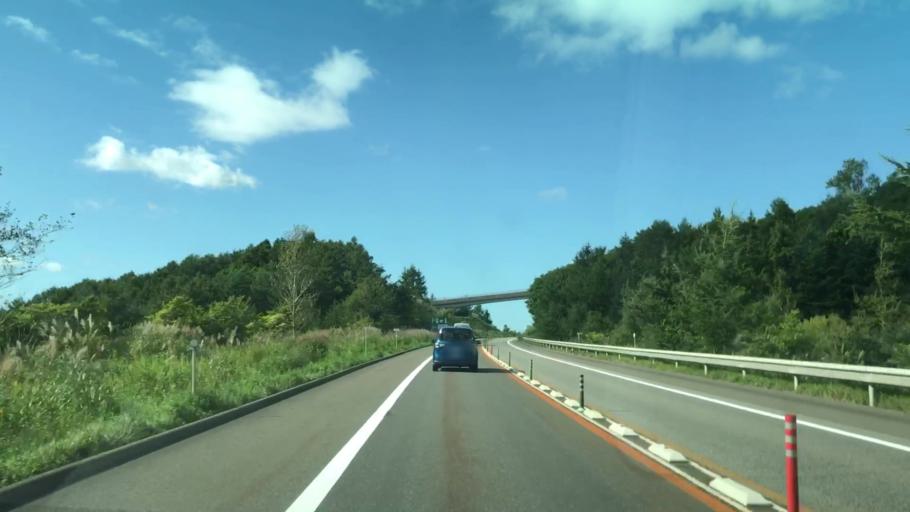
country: JP
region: Hokkaido
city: Date
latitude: 42.4437
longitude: 140.9155
